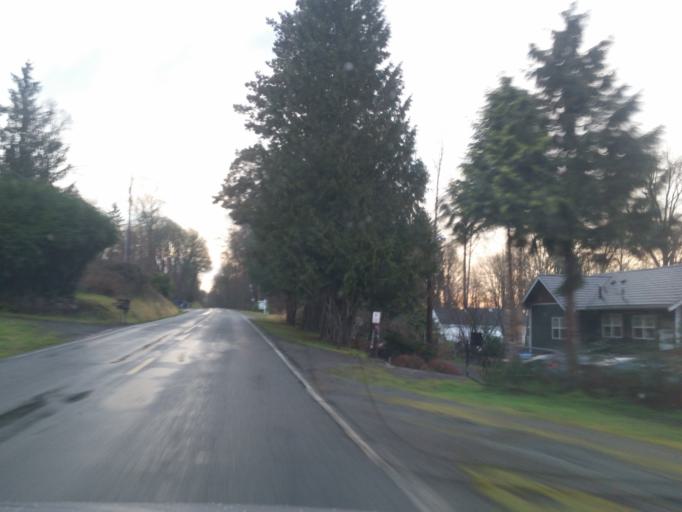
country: US
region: Washington
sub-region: Snohomish County
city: Cathcart
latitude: 47.8509
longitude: -122.0930
